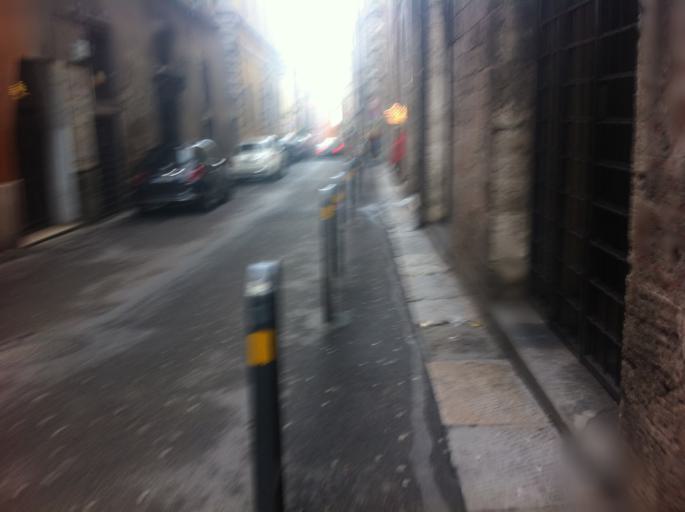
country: IT
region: Umbria
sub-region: Provincia di Perugia
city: Perugia
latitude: 43.1130
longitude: 12.3896
